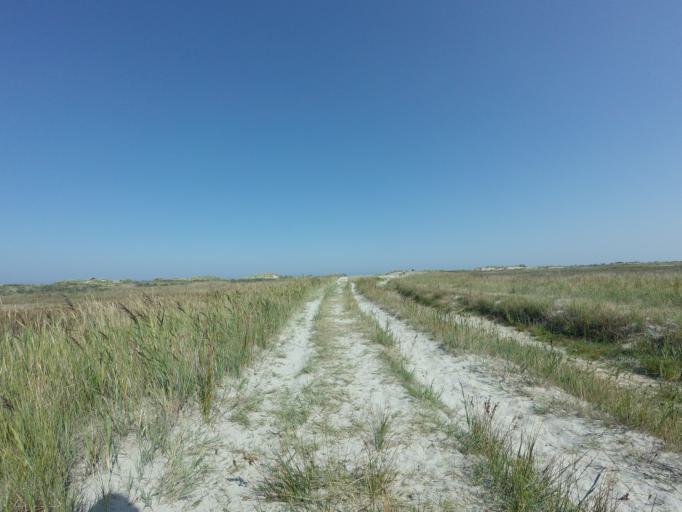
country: NL
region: Friesland
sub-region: Gemeente Schiermonnikoog
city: Schiermonnikoog
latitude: 53.5006
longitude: 6.2453
